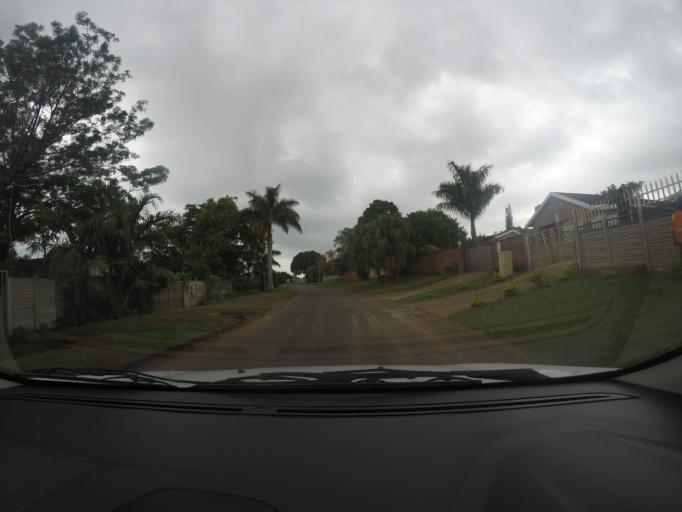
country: ZA
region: KwaZulu-Natal
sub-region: uThungulu District Municipality
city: Empangeni
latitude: -28.7637
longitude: 31.8988
